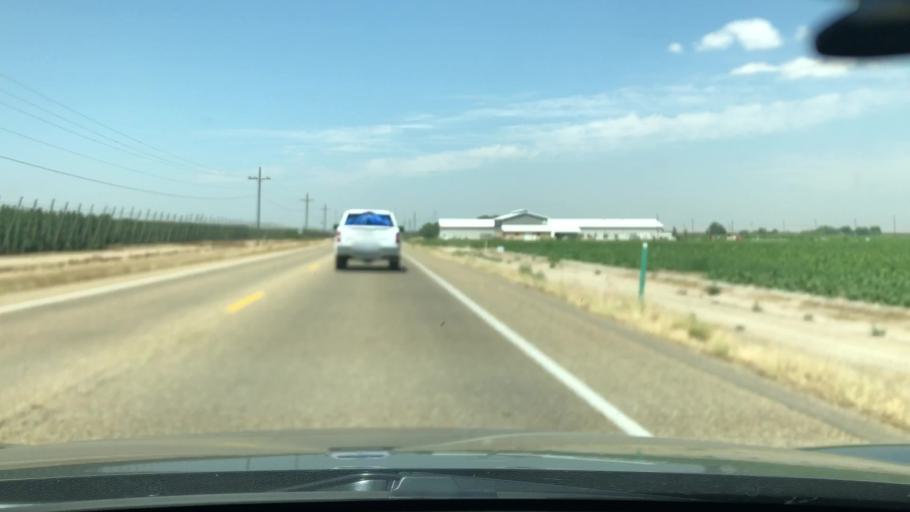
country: US
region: Idaho
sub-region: Canyon County
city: Wilder
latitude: 43.7022
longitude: -116.9120
